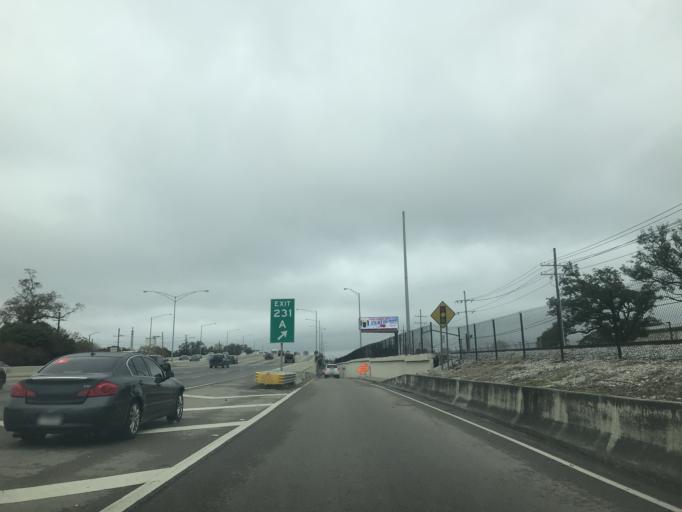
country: US
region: Louisiana
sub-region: Jefferson Parish
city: Metairie
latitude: 29.9791
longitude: -90.1127
